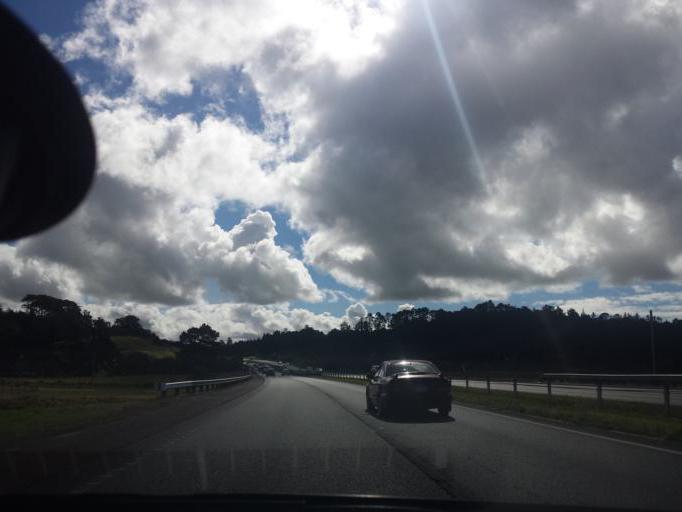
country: NZ
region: Auckland
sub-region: Auckland
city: Rothesay Bay
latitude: -36.6849
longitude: 174.7003
